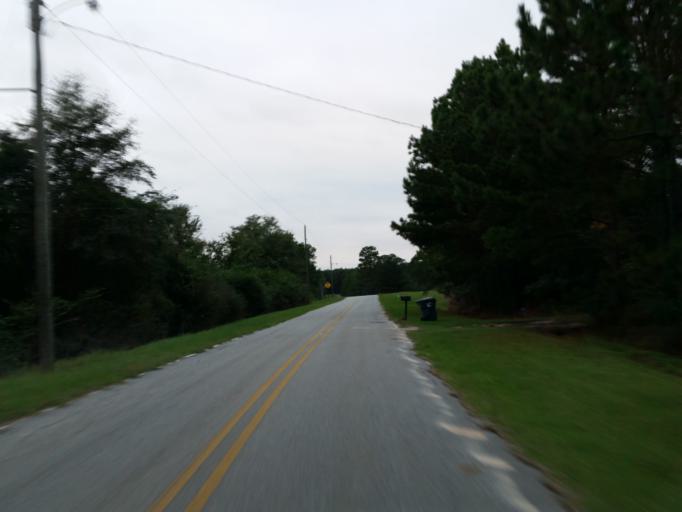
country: US
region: Georgia
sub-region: Crisp County
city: Cordele
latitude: 31.8333
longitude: -83.7444
